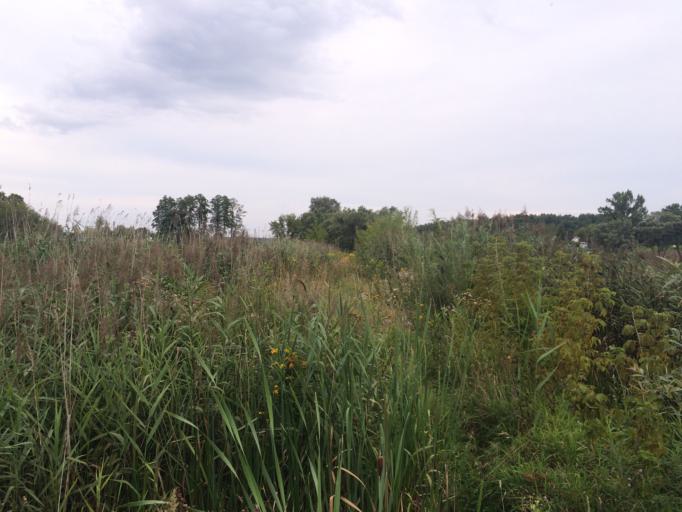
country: PL
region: Swietokrzyskie
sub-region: Powiat starachowicki
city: Starachowice
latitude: 51.0497
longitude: 21.0568
